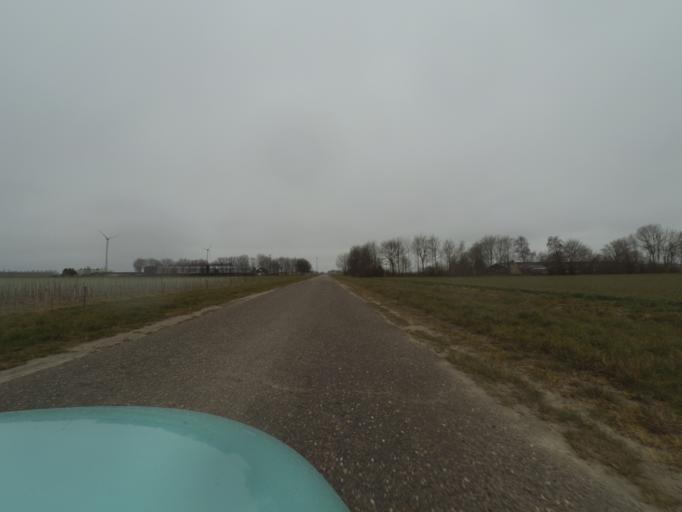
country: NL
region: Gelderland
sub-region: Gemeente Harderwijk
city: Harderwijk
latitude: 52.3928
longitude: 5.5931
